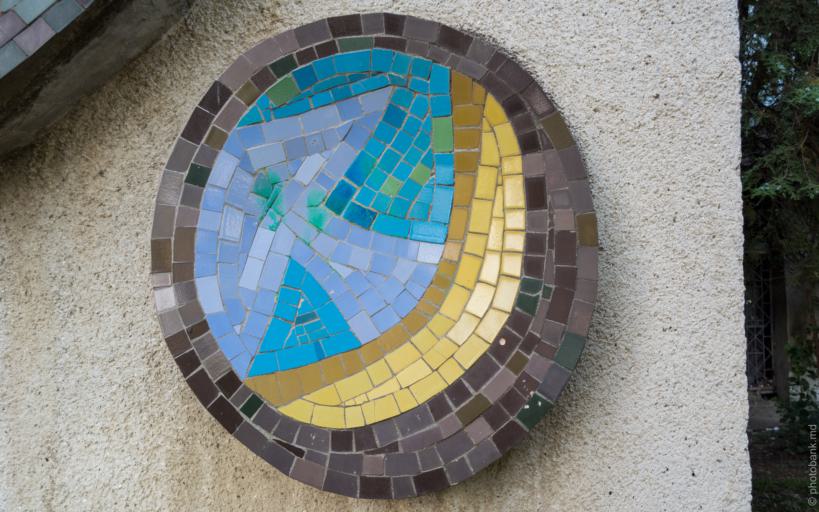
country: MD
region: Balti
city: Balti
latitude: 47.7696
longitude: 27.9425
